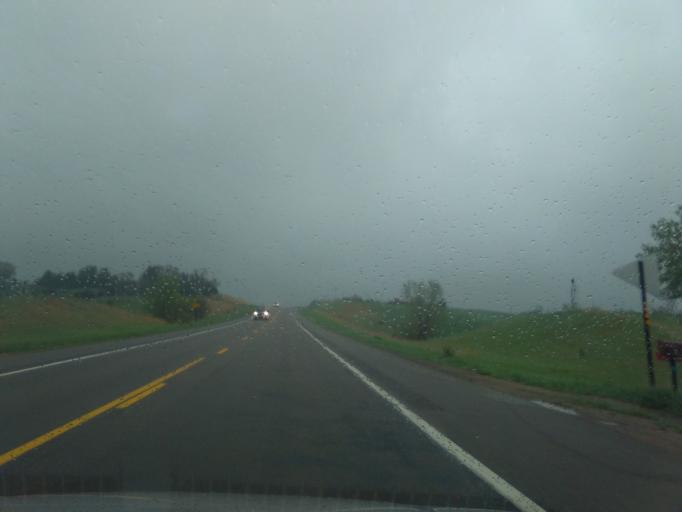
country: US
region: Nebraska
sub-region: Madison County
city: Norfolk
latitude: 42.1007
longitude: -97.3162
